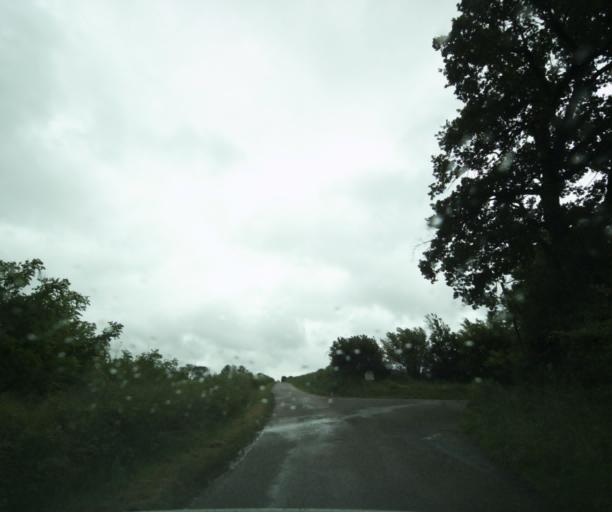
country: FR
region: Bourgogne
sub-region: Departement de Saone-et-Loire
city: Matour
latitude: 46.4652
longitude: 4.4755
